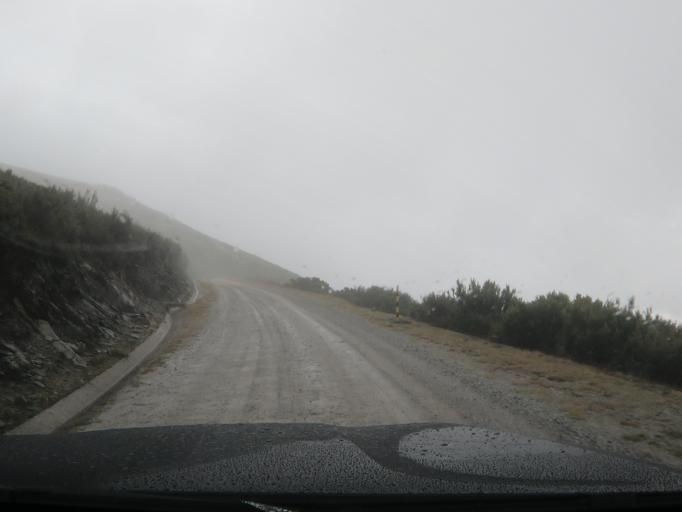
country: PT
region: Vila Real
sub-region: Vila Real
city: Vila Real
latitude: 41.3288
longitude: -7.8455
